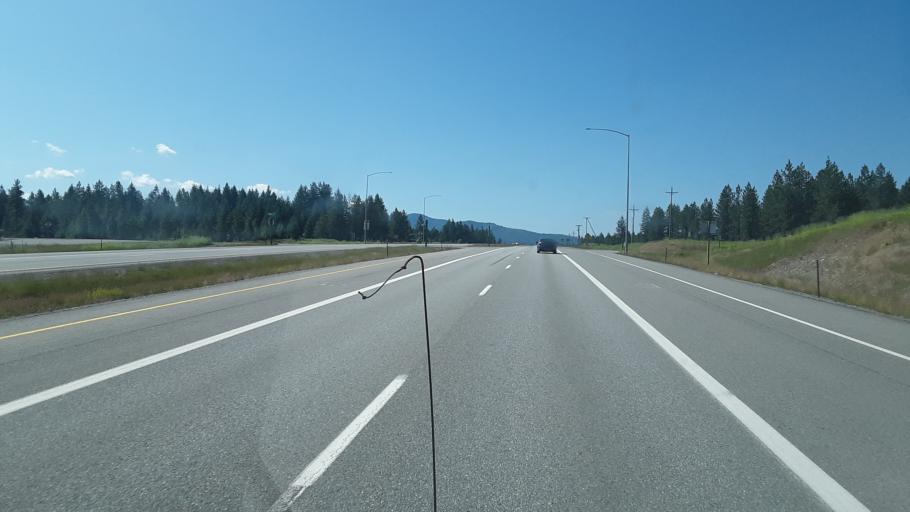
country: US
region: Idaho
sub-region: Kootenai County
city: Spirit Lake
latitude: 47.9804
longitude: -116.6994
